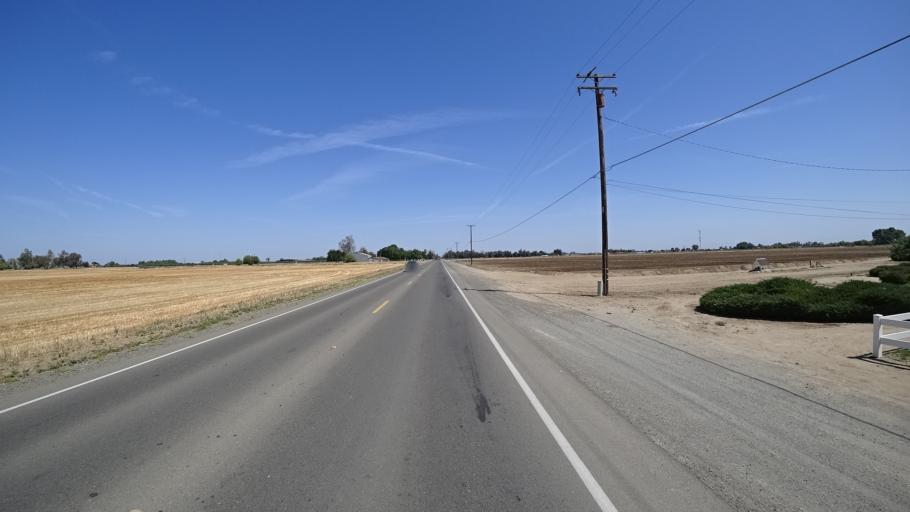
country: US
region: California
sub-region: Kings County
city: Lemoore
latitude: 36.2585
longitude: -119.7809
